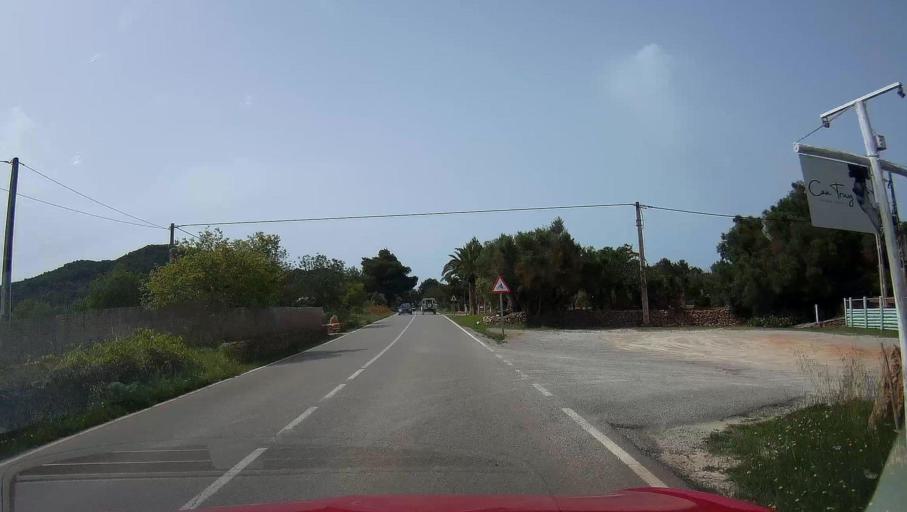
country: ES
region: Balearic Islands
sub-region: Illes Balears
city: Santa Eularia des Riu
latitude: 38.9889
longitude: 1.4882
